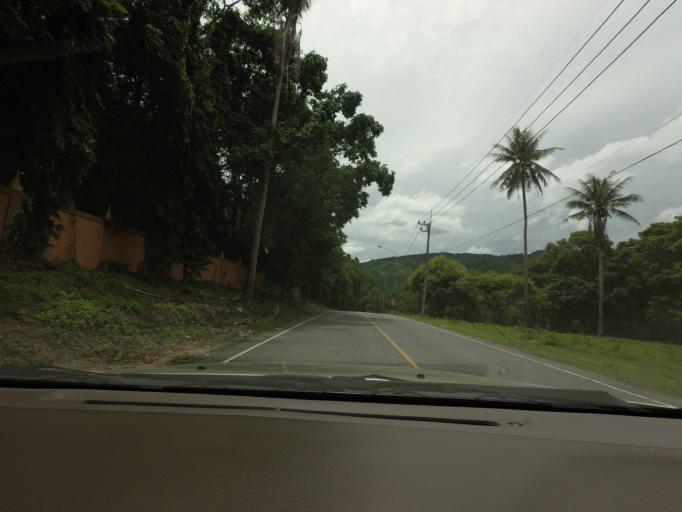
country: TH
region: Chon Buri
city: Ban Bueng
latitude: 13.2363
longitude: 101.0295
